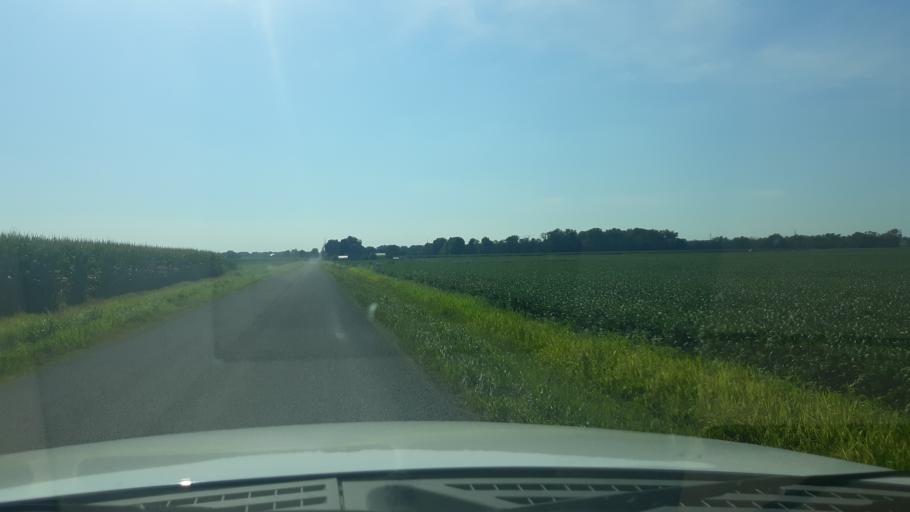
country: US
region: Illinois
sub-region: Saline County
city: Eldorado
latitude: 37.8631
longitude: -88.4969
